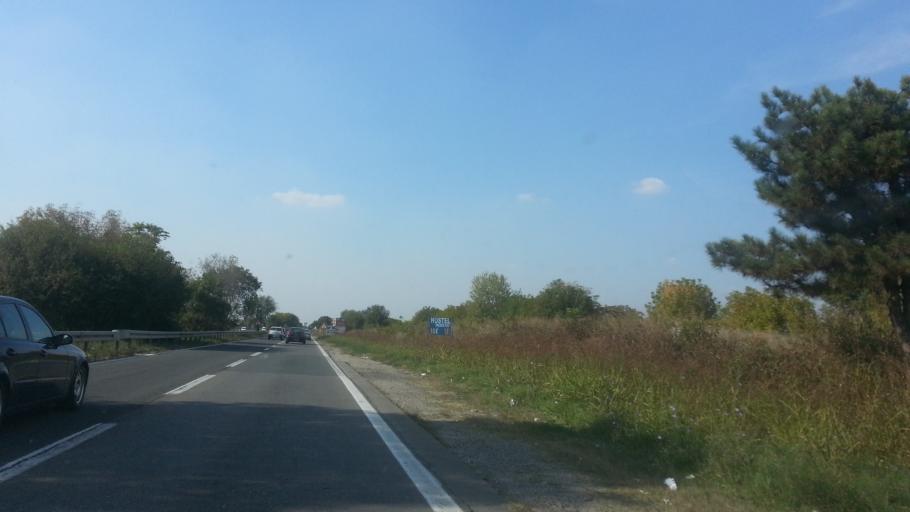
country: RS
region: Central Serbia
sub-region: Belgrade
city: Zemun
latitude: 44.8588
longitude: 20.3581
